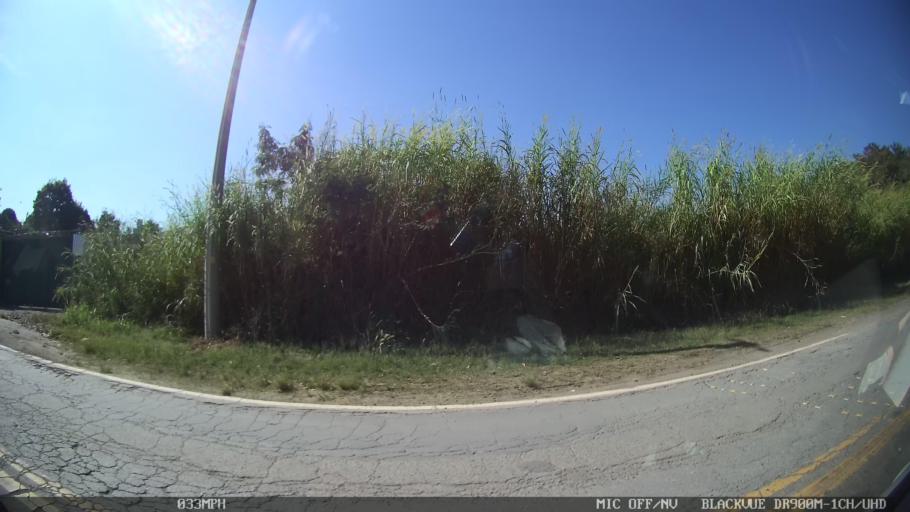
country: BR
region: Sao Paulo
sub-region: Valinhos
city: Valinhos
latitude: -22.9977
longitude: -47.0851
